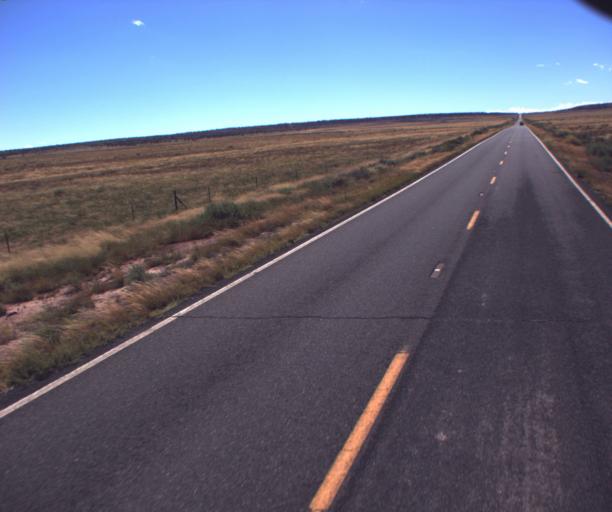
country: US
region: Arizona
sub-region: Apache County
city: Saint Johns
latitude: 34.6887
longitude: -109.2779
